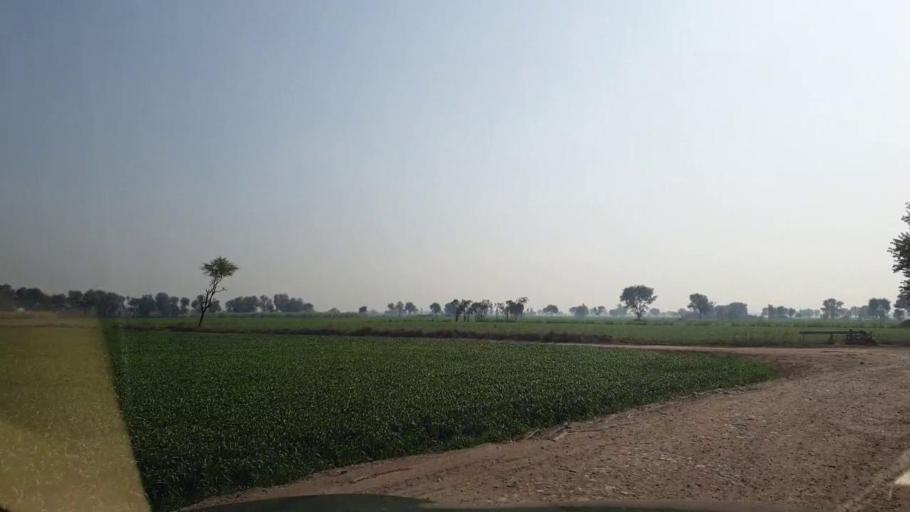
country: PK
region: Sindh
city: Ubauro
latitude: 28.1124
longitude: 69.7939
